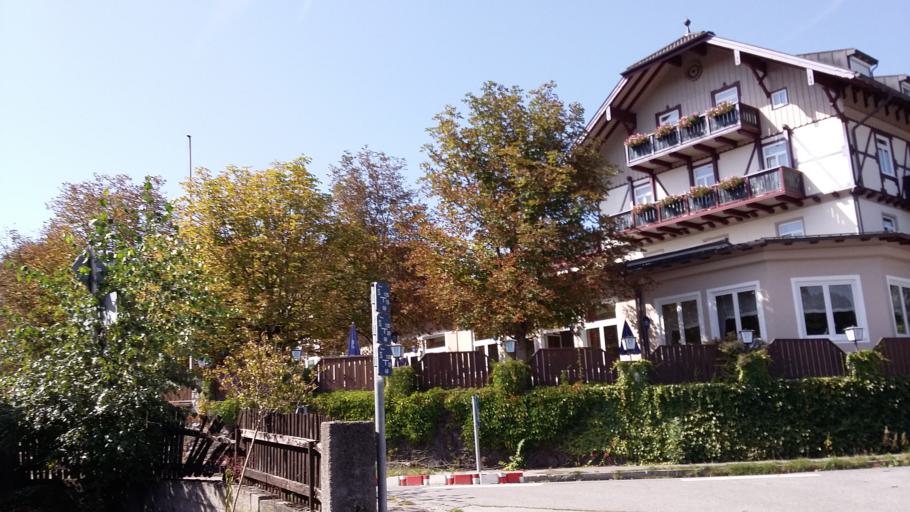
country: DE
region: Bavaria
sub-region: Upper Bavaria
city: Bernried
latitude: 47.8678
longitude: 11.2931
